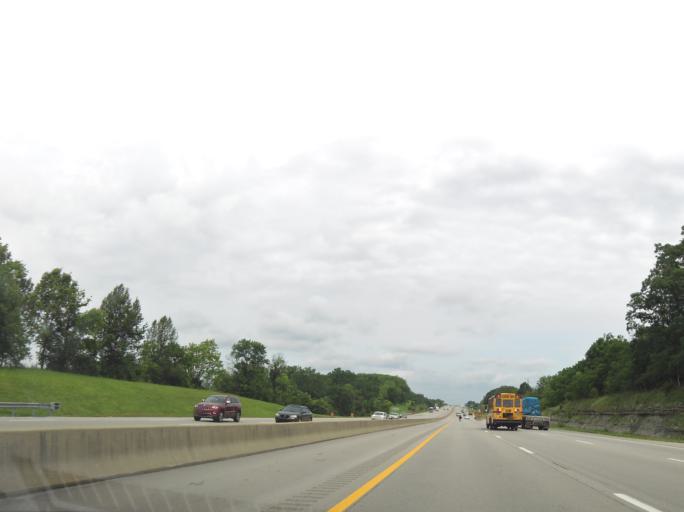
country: US
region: Kentucky
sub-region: Scott County
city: Georgetown
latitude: 38.2543
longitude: -84.5494
